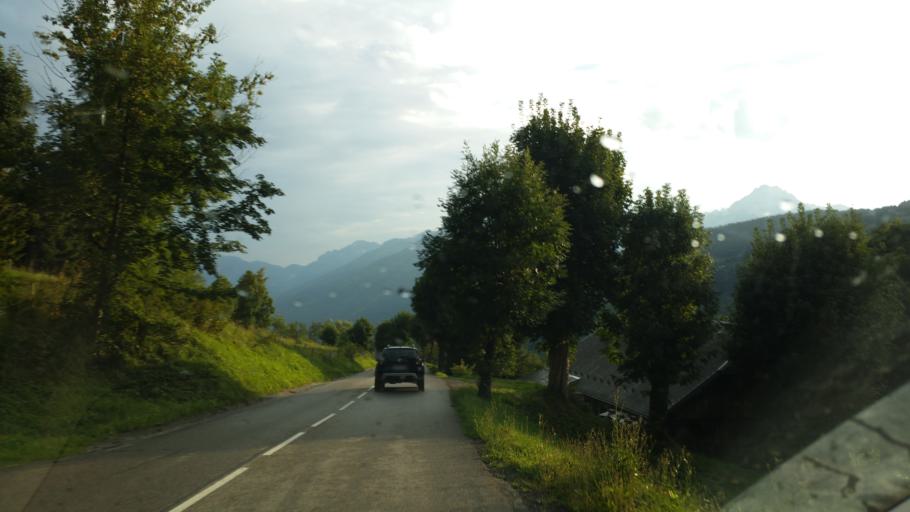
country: FR
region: Rhone-Alpes
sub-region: Departement de la Savoie
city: La Chambre
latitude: 45.3998
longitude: 6.3391
